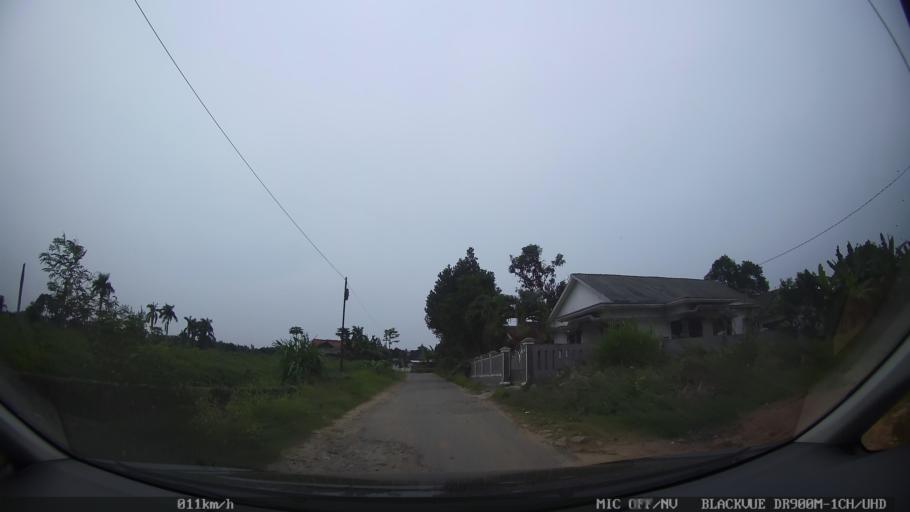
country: ID
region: Lampung
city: Panjang
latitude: -5.4100
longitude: 105.3571
